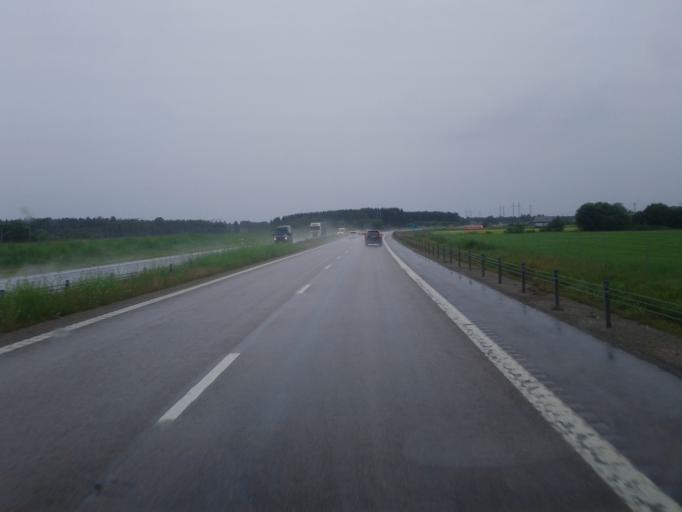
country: SE
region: Uppsala
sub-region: Tierps Kommun
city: Tierp
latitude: 60.3468
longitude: 17.4776
